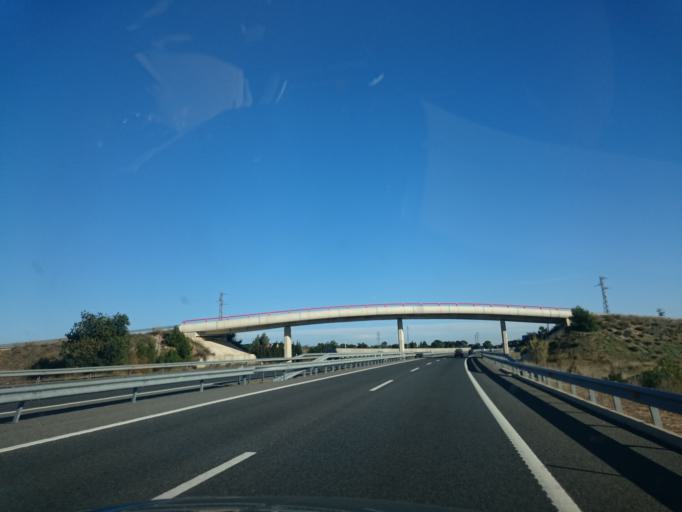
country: ES
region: Catalonia
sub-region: Provincia de Tarragona
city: Cambrils
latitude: 41.0754
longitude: 1.0172
